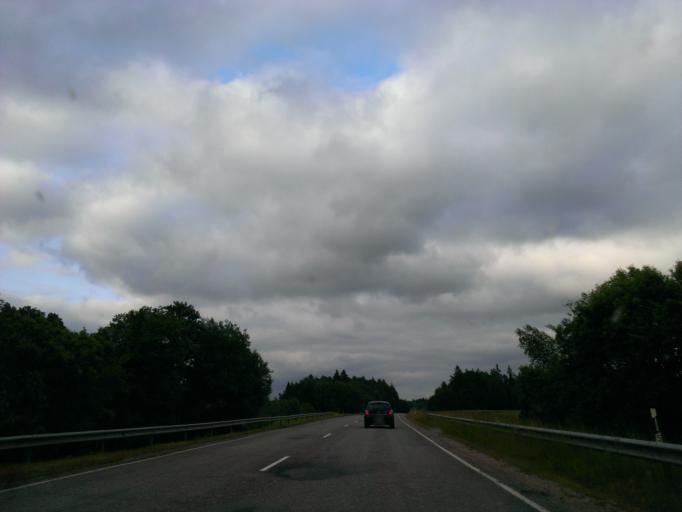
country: LV
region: Saldus Rajons
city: Saldus
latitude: 56.6721
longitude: 22.3781
